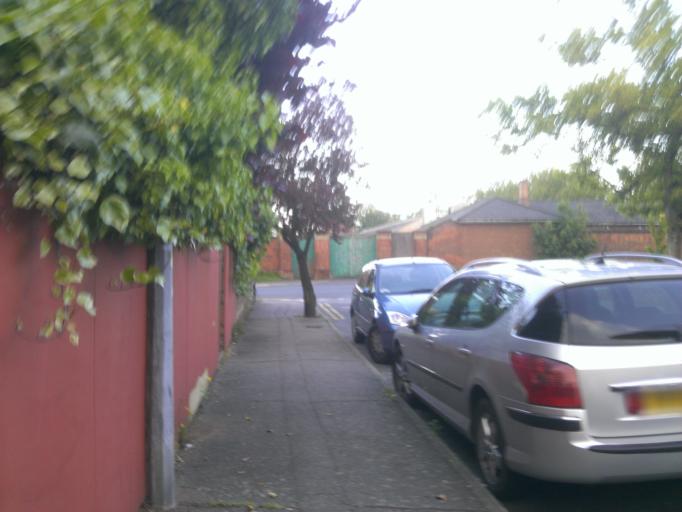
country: GB
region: England
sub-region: Essex
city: Colchester
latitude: 51.8823
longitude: 0.8892
